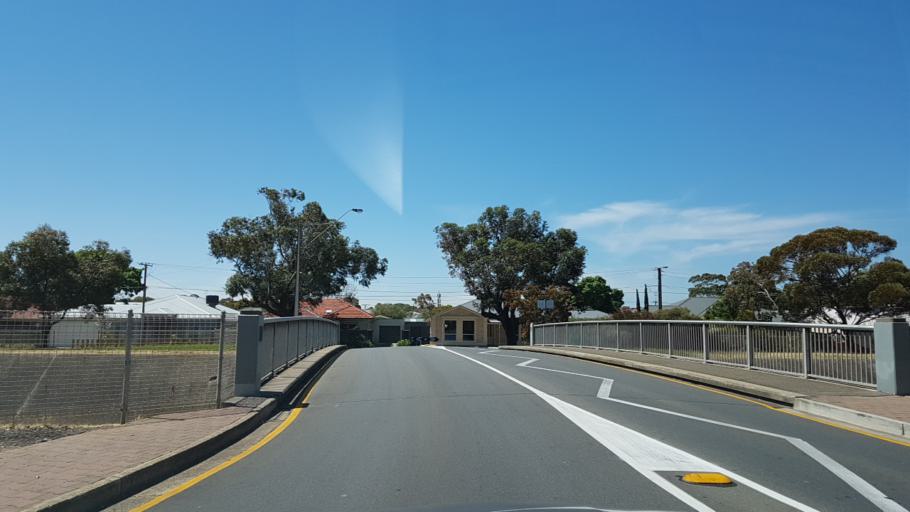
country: AU
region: South Australia
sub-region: Holdfast Bay
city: Glenelg East
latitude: -34.9684
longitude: 138.5221
